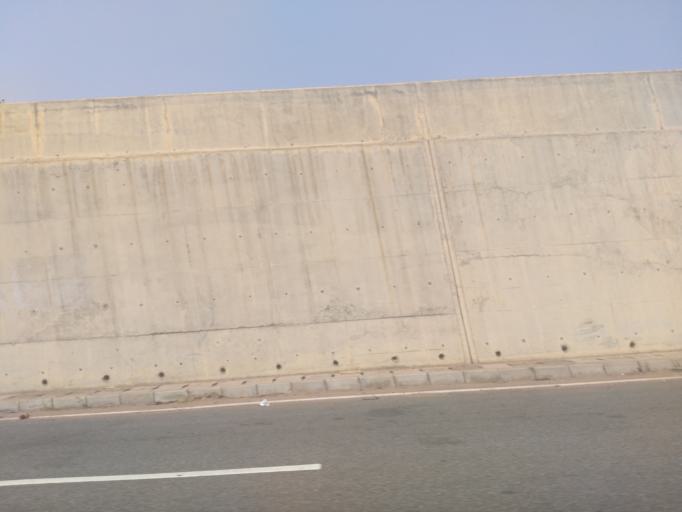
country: GH
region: Greater Accra
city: Dome
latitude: 5.6156
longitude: -0.2114
